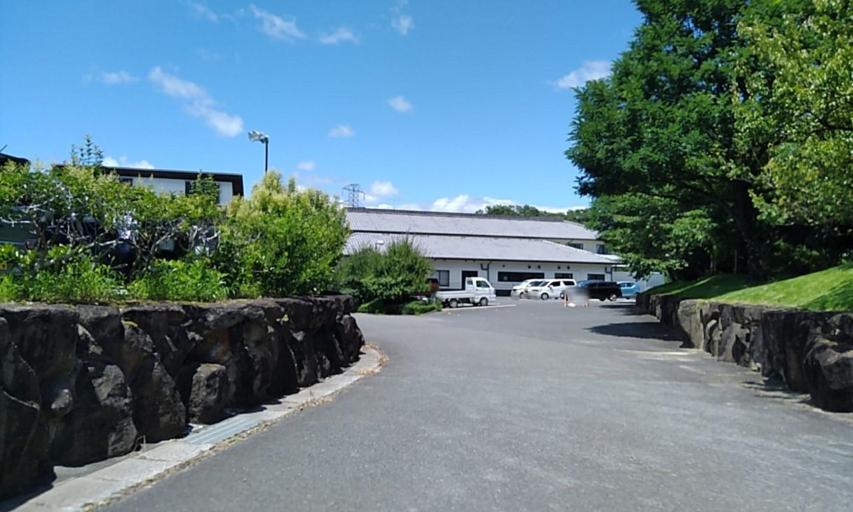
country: JP
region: Mie
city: Ueno-ebisumachi
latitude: 34.7145
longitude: 136.0474
